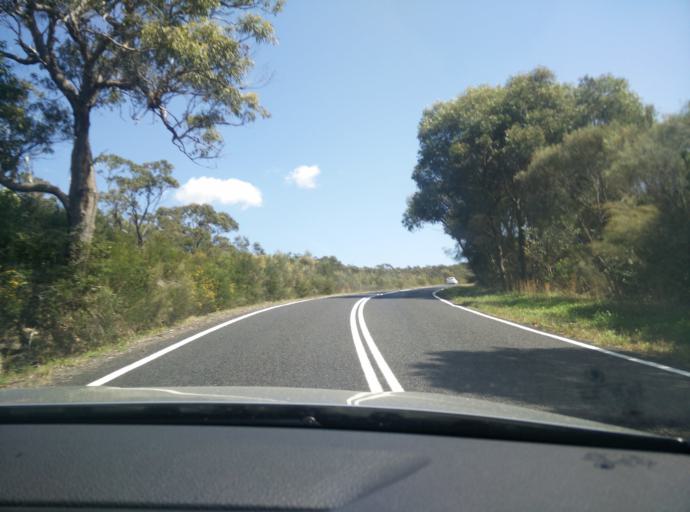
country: AU
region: New South Wales
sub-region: Gosford Shire
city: Umina
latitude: -33.5380
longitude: 151.2928
